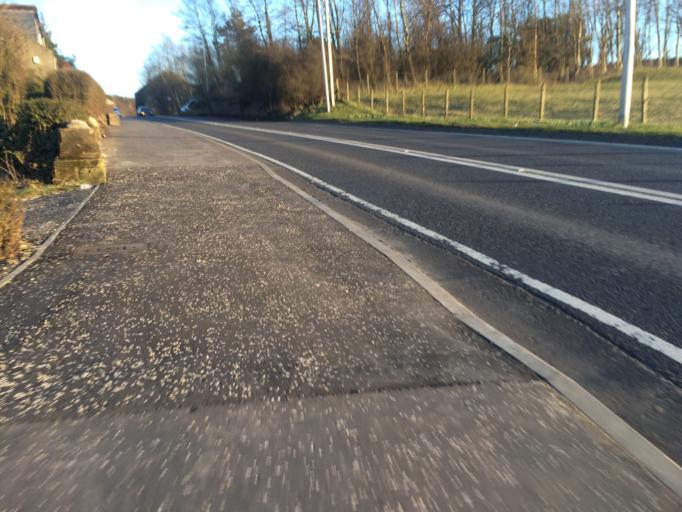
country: GB
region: Scotland
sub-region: Fife
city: Lochgelly
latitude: 56.1410
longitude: -3.3204
